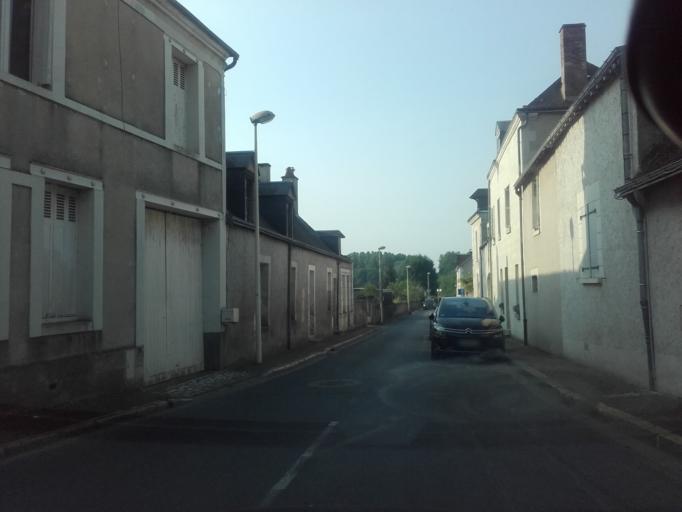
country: FR
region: Centre
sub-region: Departement d'Indre-et-Loire
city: Noizay
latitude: 47.4212
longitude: 0.8918
